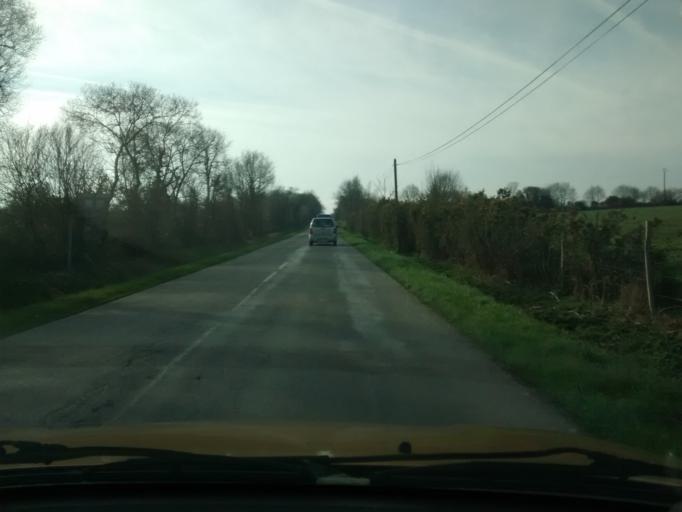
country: FR
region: Pays de la Loire
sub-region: Departement de la Loire-Atlantique
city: Notre-Dame-des-Landes
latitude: 47.3665
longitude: -1.7298
